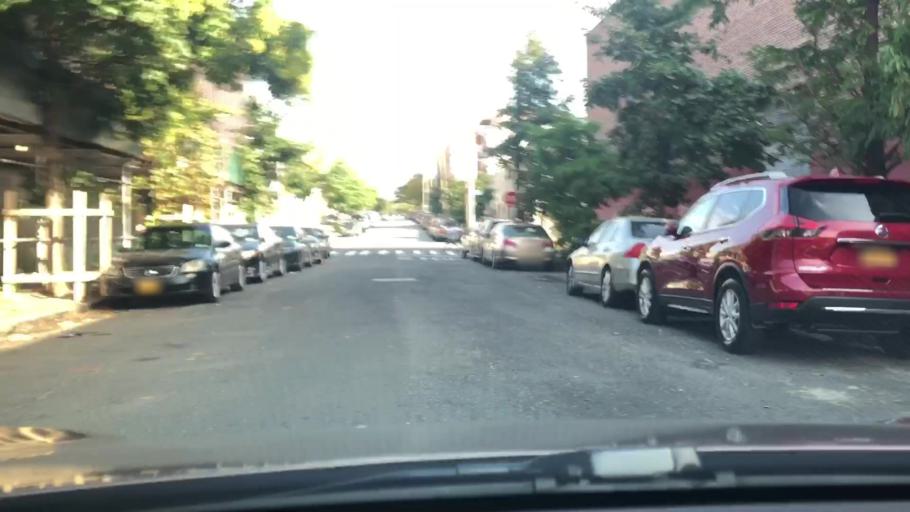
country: US
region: New York
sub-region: Bronx
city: The Bronx
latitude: 40.8088
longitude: -73.9087
